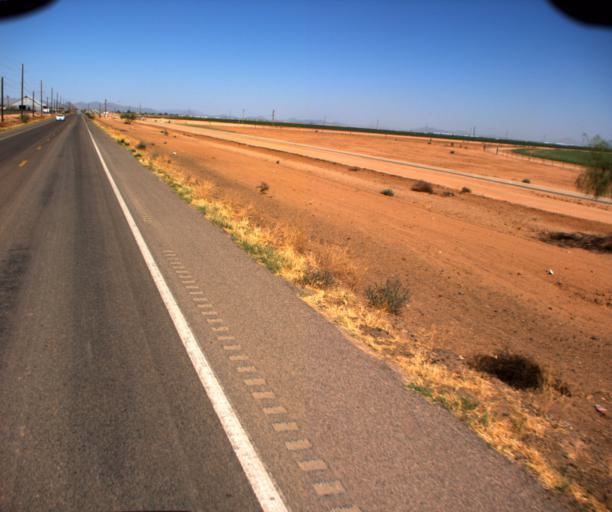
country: US
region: Arizona
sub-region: Pinal County
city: Casa Grande
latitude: 32.8794
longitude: -111.9172
